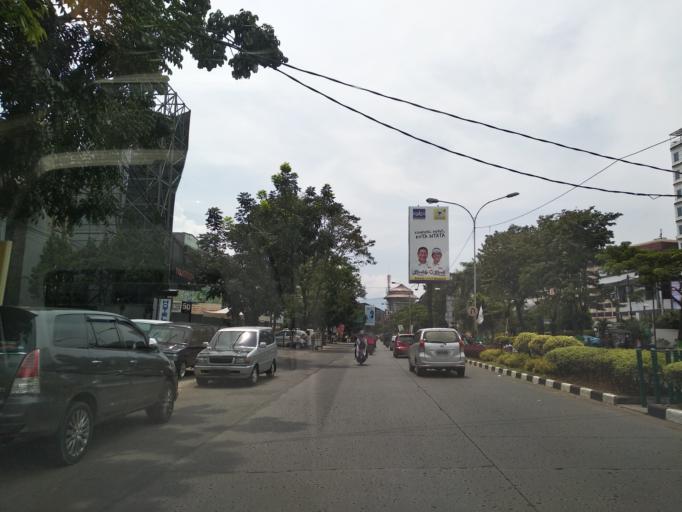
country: ID
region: West Java
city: Bandung
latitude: -6.9363
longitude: 107.6233
